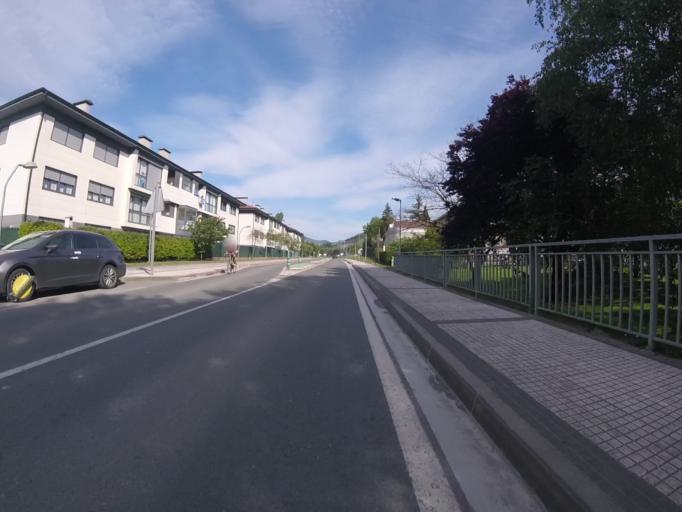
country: ES
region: Basque Country
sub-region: Provincia de Guipuzcoa
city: Gabiria
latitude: 43.0648
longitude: -2.2764
